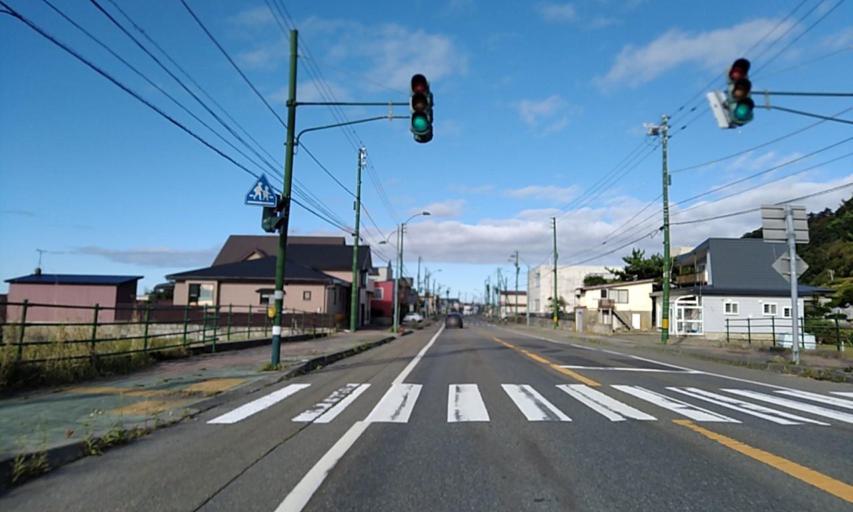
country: JP
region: Hokkaido
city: Shizunai-furukawacho
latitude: 42.2478
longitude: 142.5635
